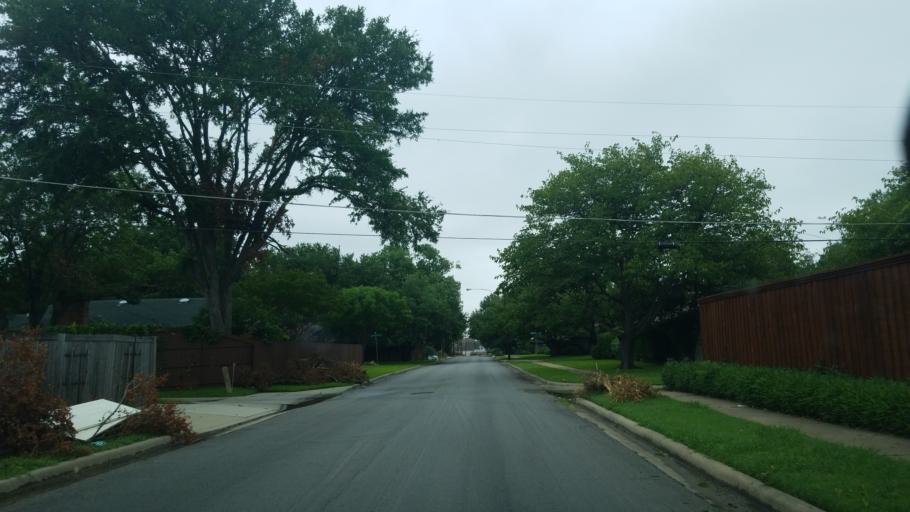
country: US
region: Texas
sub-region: Dallas County
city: Farmers Branch
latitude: 32.8925
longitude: -96.8730
